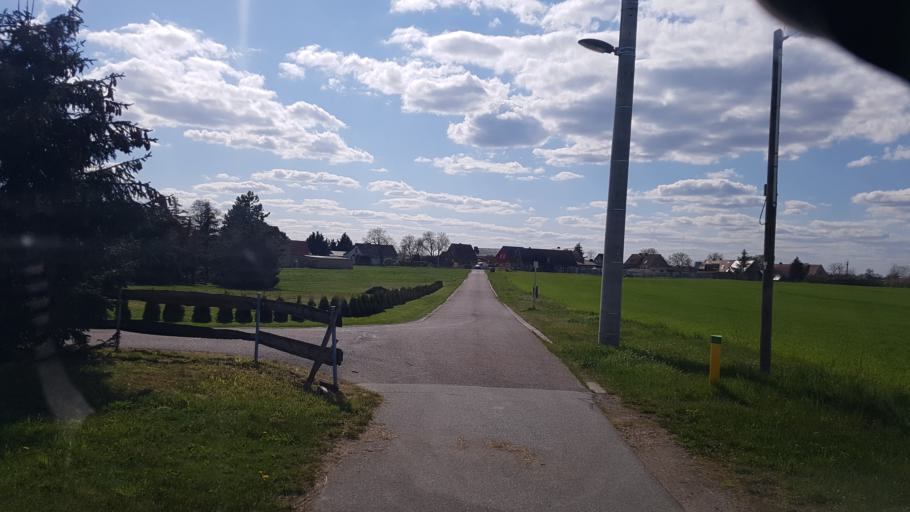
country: DE
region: Brandenburg
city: Muhlberg
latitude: 51.4566
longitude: 13.2636
